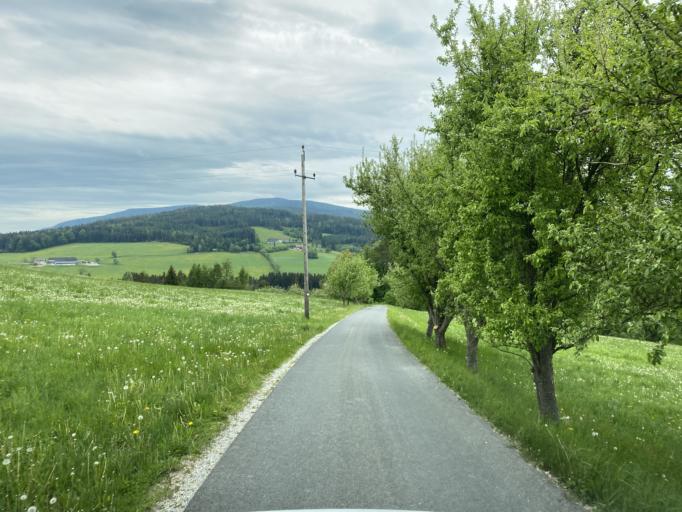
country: AT
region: Styria
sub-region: Politischer Bezirk Weiz
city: Gschaid bei Birkfeld
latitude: 47.3473
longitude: 15.7363
